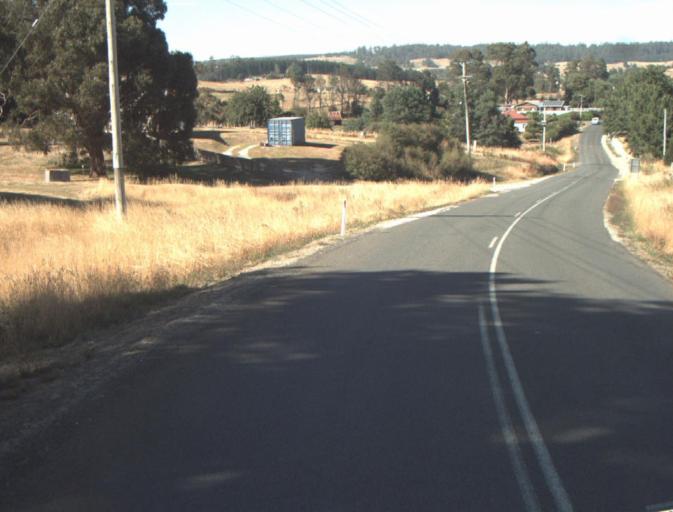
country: AU
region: Tasmania
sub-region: Launceston
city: Mayfield
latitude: -41.1748
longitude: 147.2299
